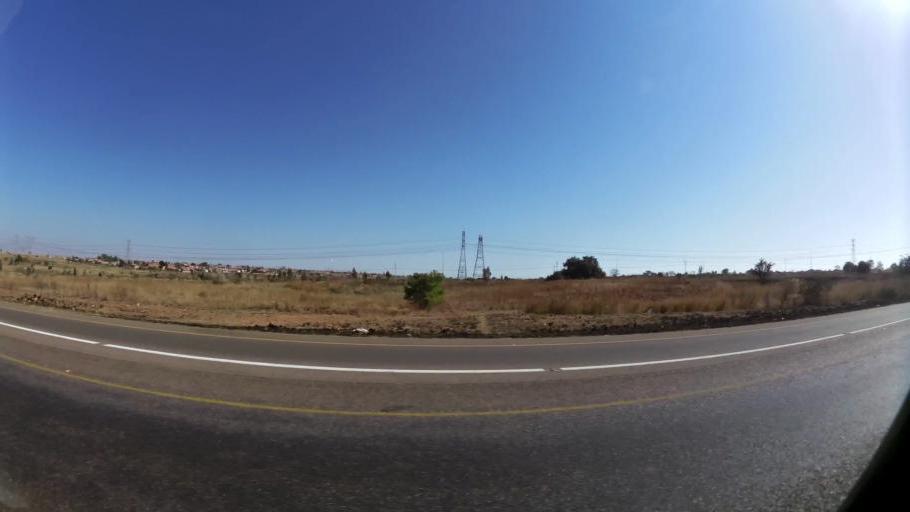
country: ZA
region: Gauteng
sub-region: City of Tshwane Metropolitan Municipality
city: Mabopane
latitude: -25.5522
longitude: 28.1090
